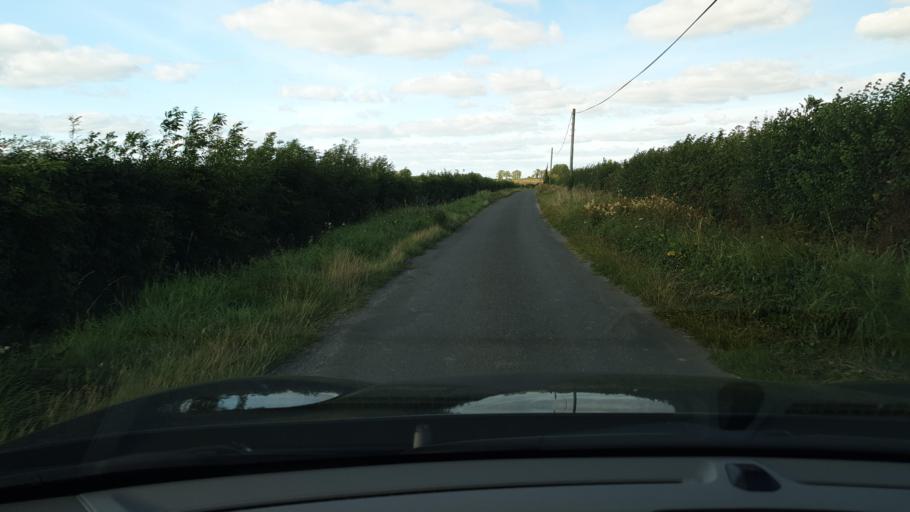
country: IE
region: Leinster
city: Hartstown
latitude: 53.4394
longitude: -6.4307
